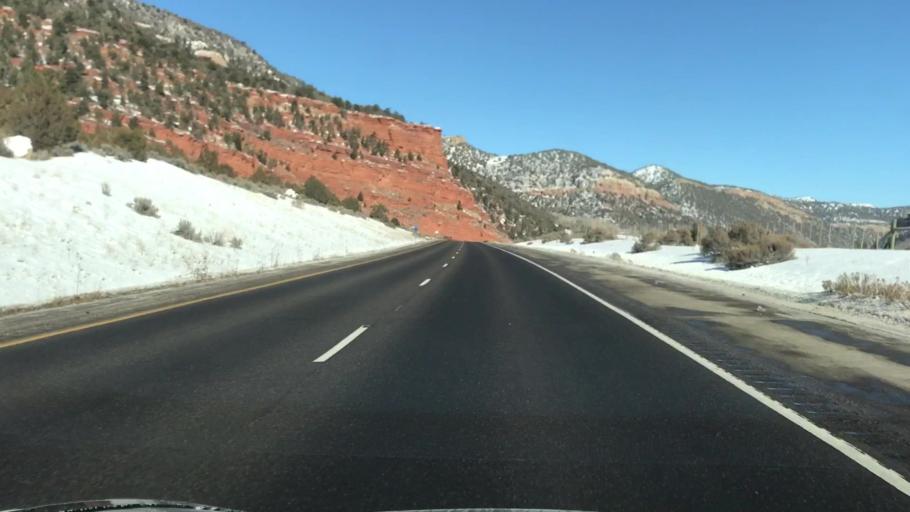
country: US
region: Colorado
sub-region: Eagle County
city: Eagle
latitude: 39.7016
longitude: -106.7316
